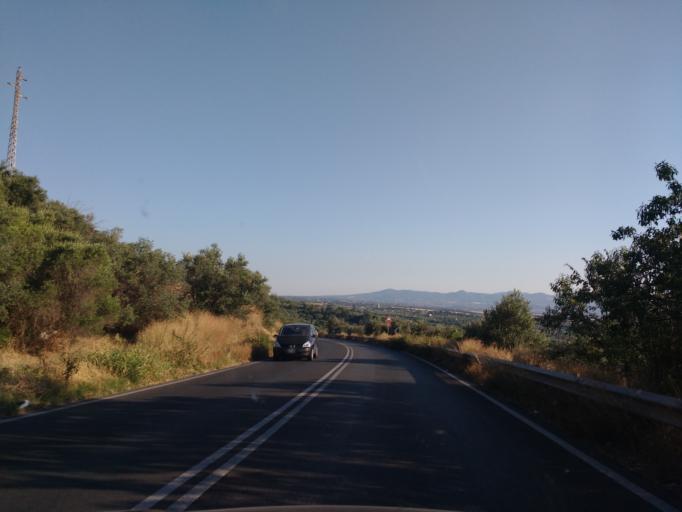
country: IT
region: Latium
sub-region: Citta metropolitana di Roma Capitale
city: Tivoli
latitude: 41.9508
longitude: 12.7909
